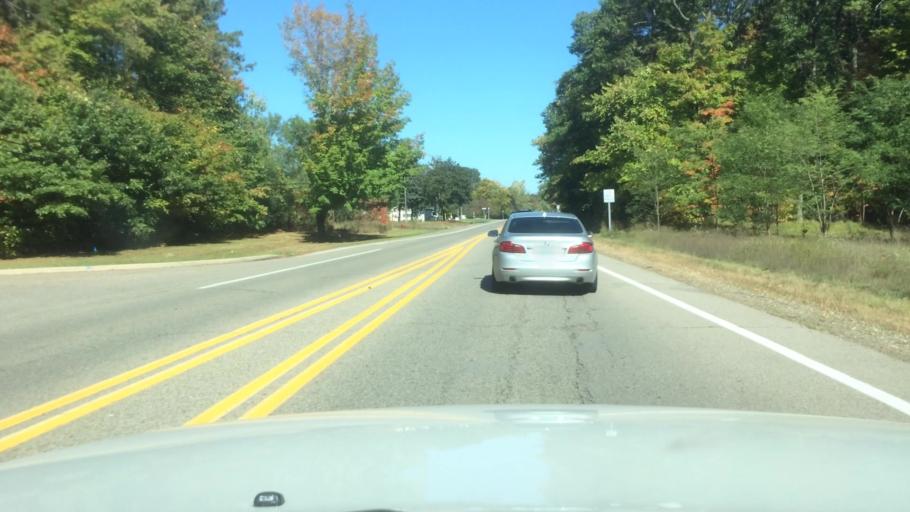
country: US
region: Michigan
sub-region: Oakland County
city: Wolverine Lake
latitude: 42.5733
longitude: -83.4500
